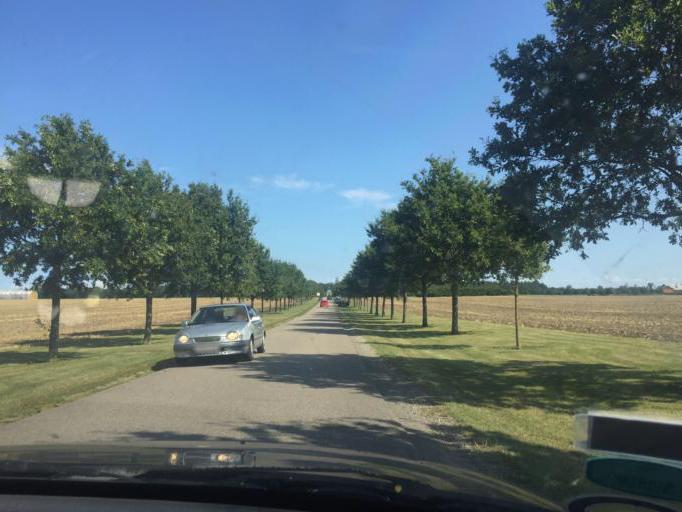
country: DK
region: Zealand
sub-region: Lolland Kommune
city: Maribo
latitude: 54.8030
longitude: 11.5079
